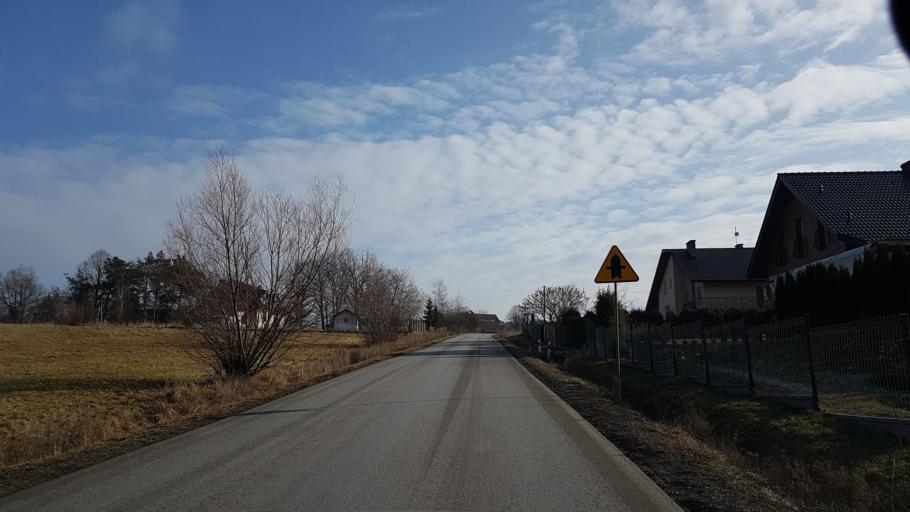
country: PL
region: Lesser Poland Voivodeship
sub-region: Powiat limanowski
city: Lukowica
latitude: 49.6390
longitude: 20.5111
